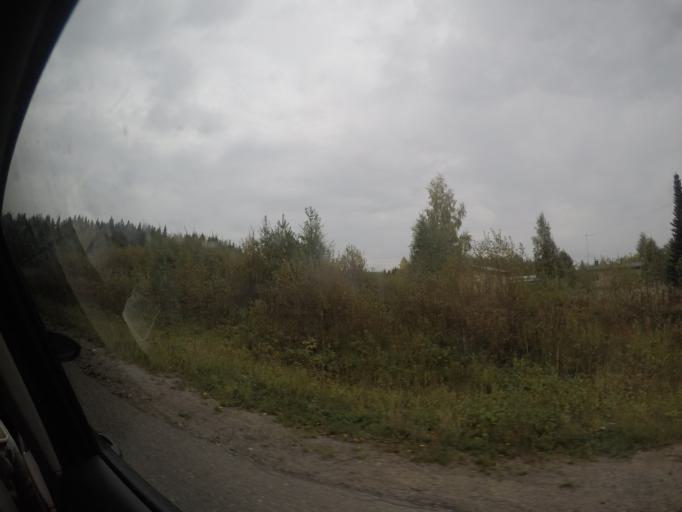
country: FI
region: Pirkanmaa
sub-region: Ylae-Pirkanmaa
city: Juupajoki
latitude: 61.8406
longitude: 24.2893
